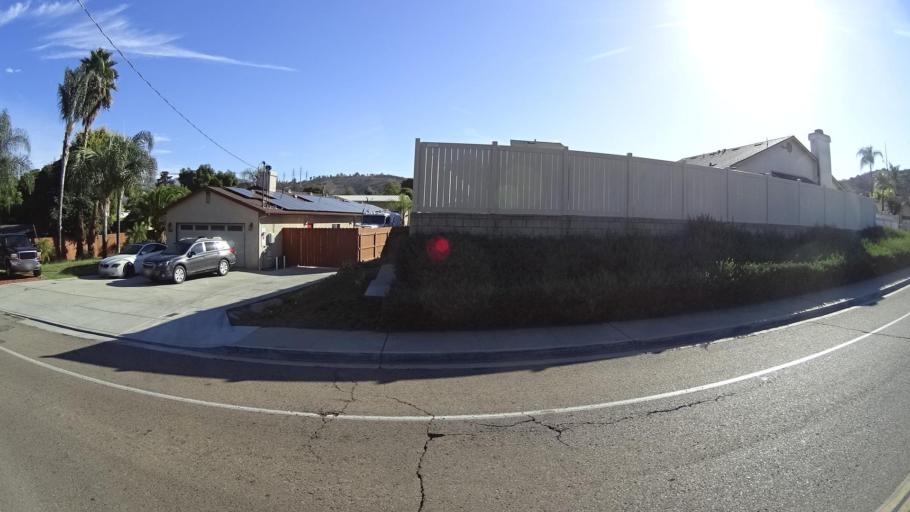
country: US
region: California
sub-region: San Diego County
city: Lakeside
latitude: 32.8552
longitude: -116.9052
